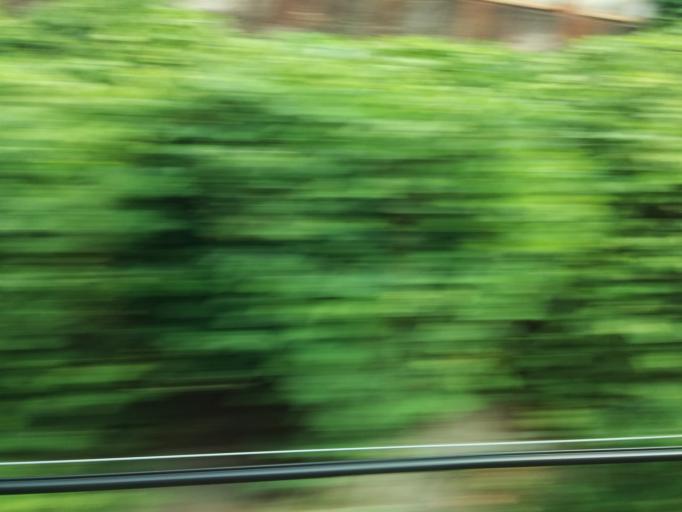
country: JP
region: Kanagawa
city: Minami-rinkan
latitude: 35.4242
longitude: 139.4476
